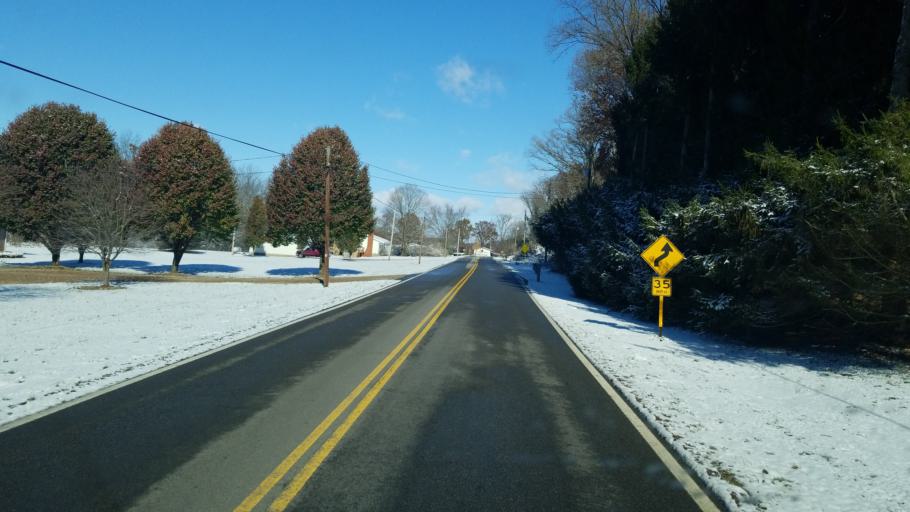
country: US
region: Ohio
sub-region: Licking County
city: Newark
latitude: 40.1487
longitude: -82.3405
